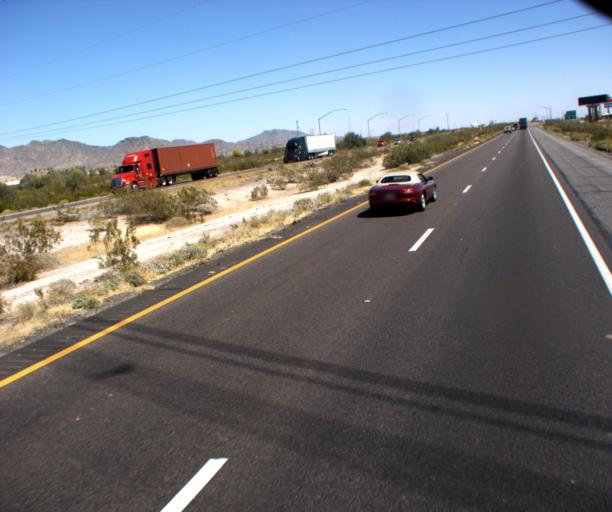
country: US
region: Arizona
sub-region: Maricopa County
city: Buckeye
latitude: 33.4305
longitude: -112.5998
